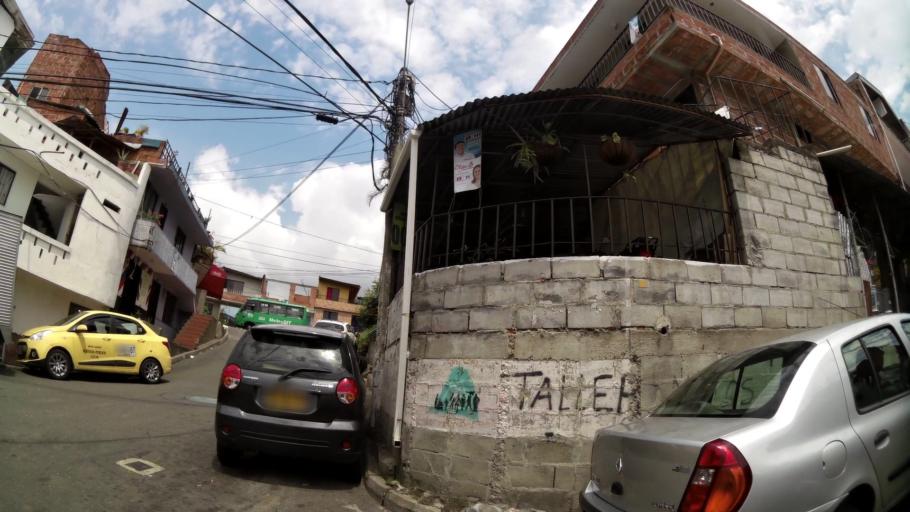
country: CO
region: Antioquia
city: Medellin
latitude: 6.2486
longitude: -75.6204
